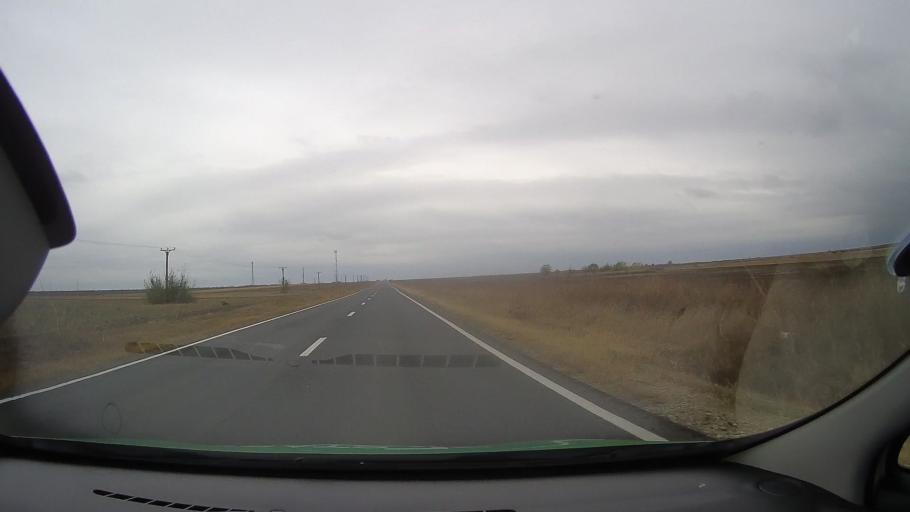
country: RO
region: Constanta
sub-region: Comuna Nicolae Balcescu
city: Nicolae Balcescu
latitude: 44.3764
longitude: 28.4202
